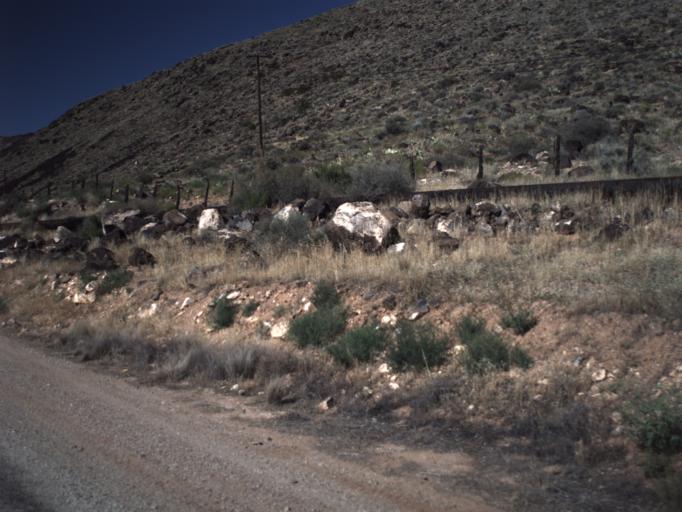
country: US
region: Utah
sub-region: Washington County
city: Toquerville
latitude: 37.2460
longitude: -113.2838
